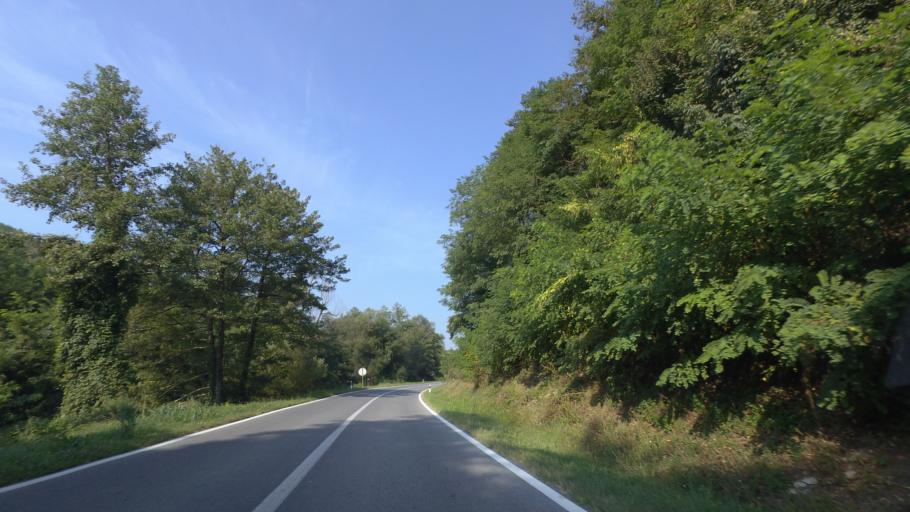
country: HR
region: Bjelovarsko-Bilogorska
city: Sirac
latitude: 45.4669
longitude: 17.2504
